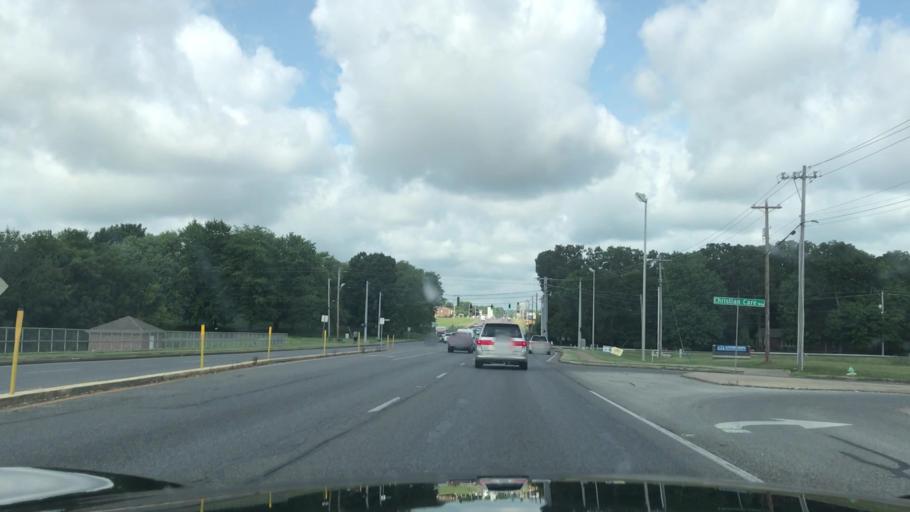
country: US
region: Kentucky
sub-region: Warren County
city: Bowling Green
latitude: 36.9605
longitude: -86.4528
